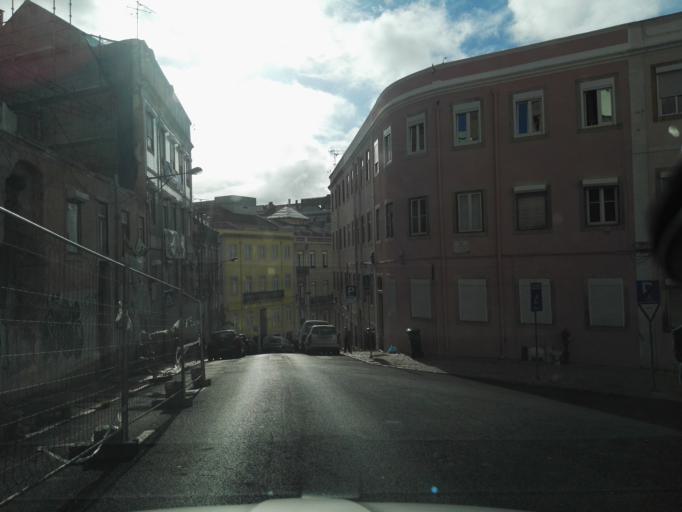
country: PT
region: Lisbon
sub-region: Lisbon
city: Lisbon
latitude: 38.7298
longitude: -9.1336
